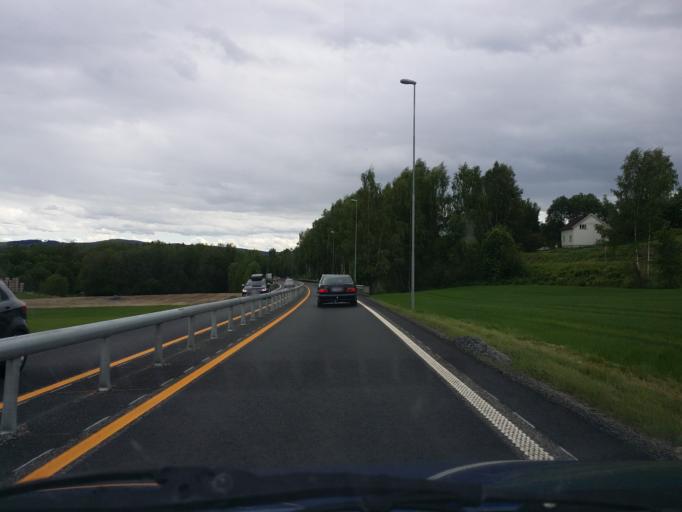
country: NO
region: Hedmark
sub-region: Ringsaker
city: Moelv
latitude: 60.9687
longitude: 10.6001
